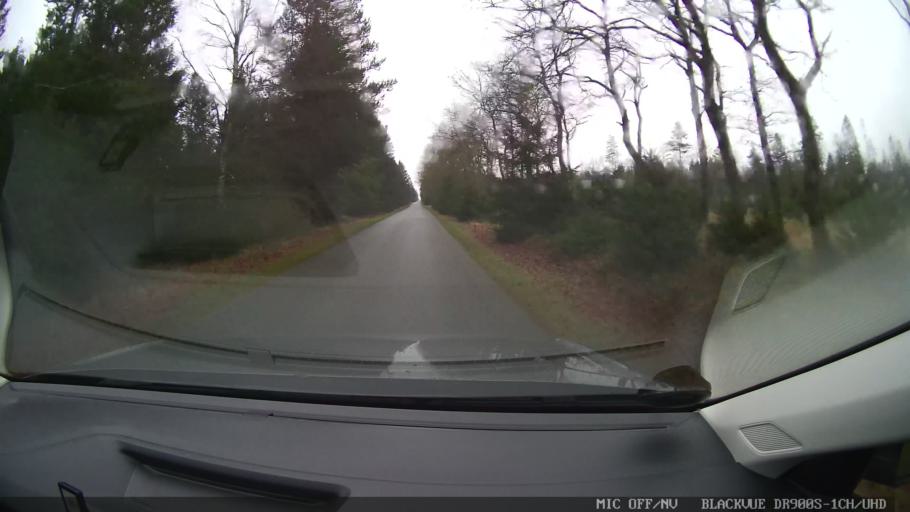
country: DK
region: Central Jutland
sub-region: Viborg Kommune
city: Karup
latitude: 56.2365
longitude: 9.1257
